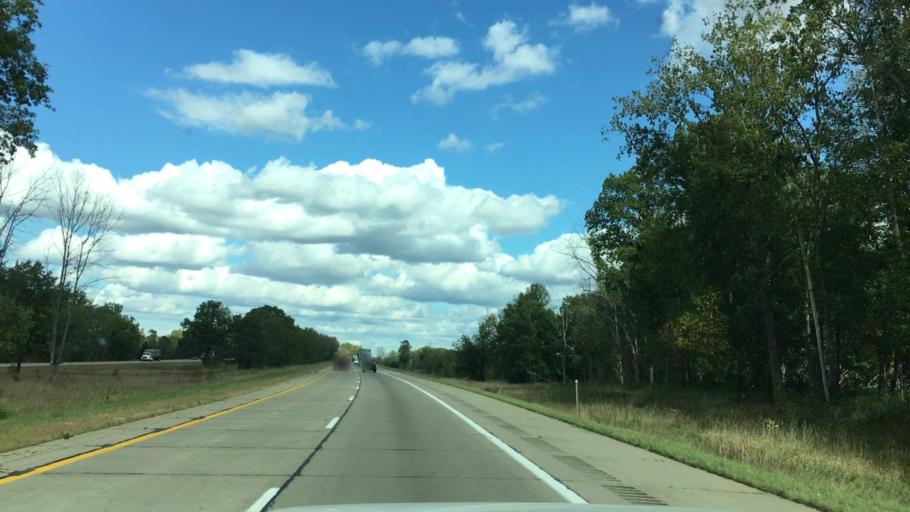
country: US
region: Michigan
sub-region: Eaton County
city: Olivet
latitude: 42.4656
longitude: -84.9022
